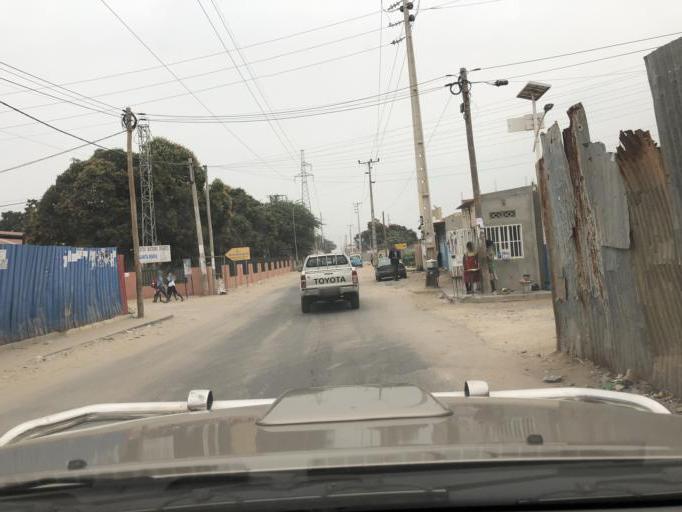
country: AO
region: Luanda
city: Luanda
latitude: -8.8865
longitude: 13.1856
